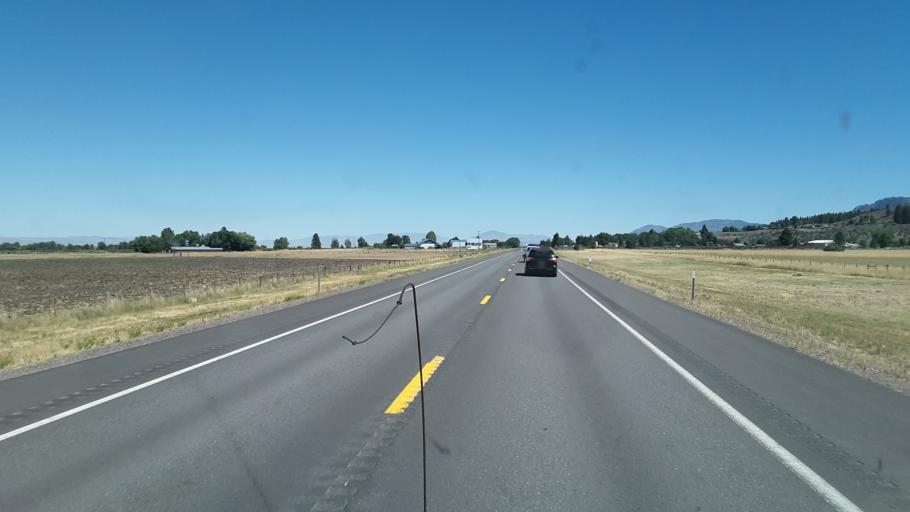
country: US
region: California
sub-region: Lassen County
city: Janesville
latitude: 40.2984
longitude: -120.5154
